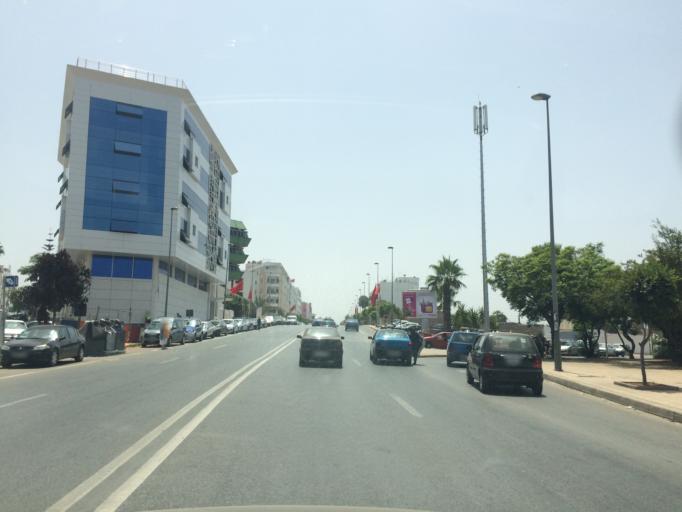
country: MA
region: Rabat-Sale-Zemmour-Zaer
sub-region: Rabat
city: Rabat
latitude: 33.9994
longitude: -6.8511
